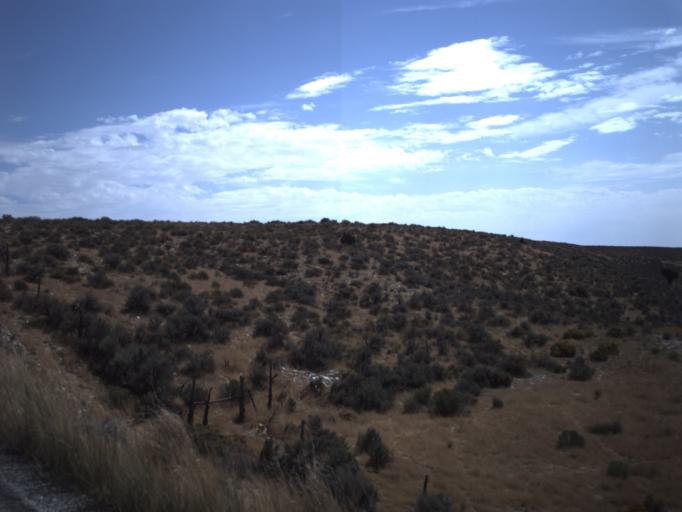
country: US
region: Idaho
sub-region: Cassia County
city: Burley
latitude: 41.8154
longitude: -113.2241
